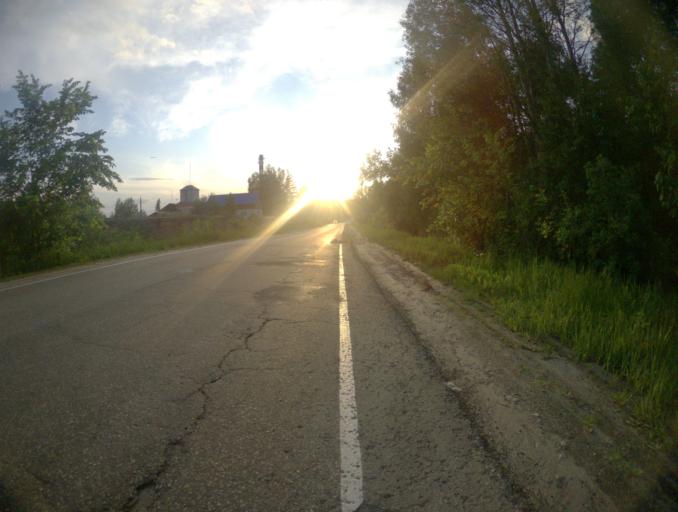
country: RU
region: Vladimir
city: Gus'-Khrustal'nyy
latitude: 55.6357
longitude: 40.7157
